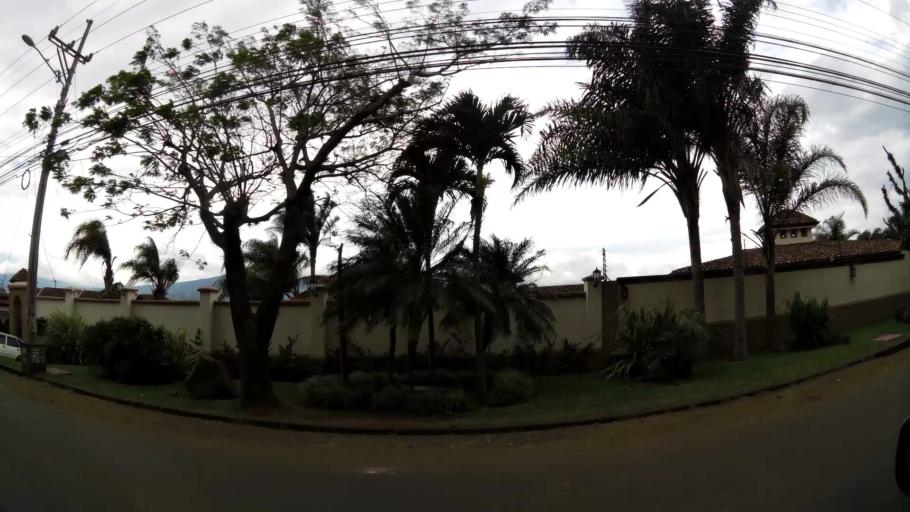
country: CR
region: Heredia
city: La Asuncion
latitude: 9.9571
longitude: -84.1692
